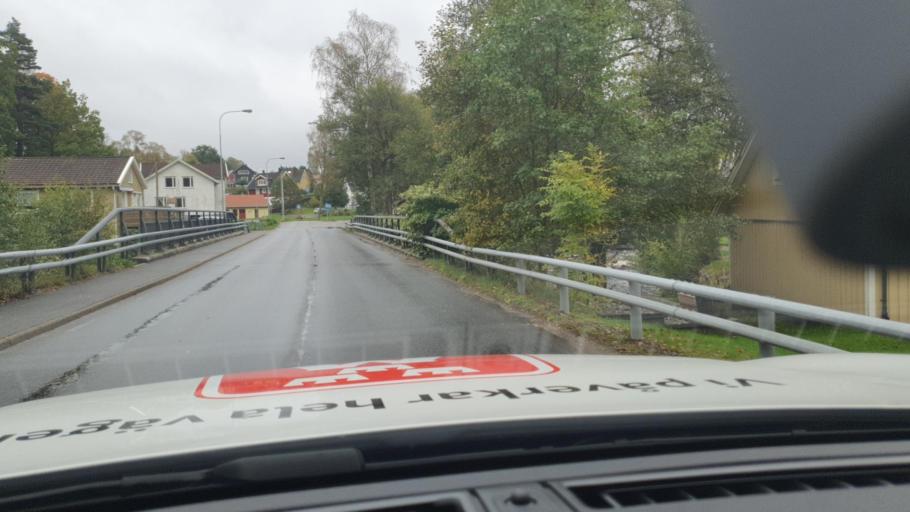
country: SE
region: Vaestra Goetaland
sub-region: Marks Kommun
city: Kinna
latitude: 57.3887
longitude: 12.6780
